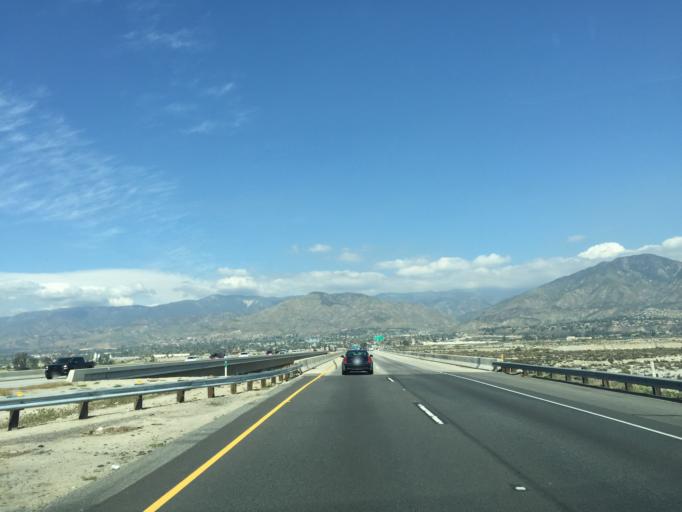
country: US
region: California
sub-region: San Bernardino County
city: Highland
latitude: 34.0920
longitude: -117.2005
